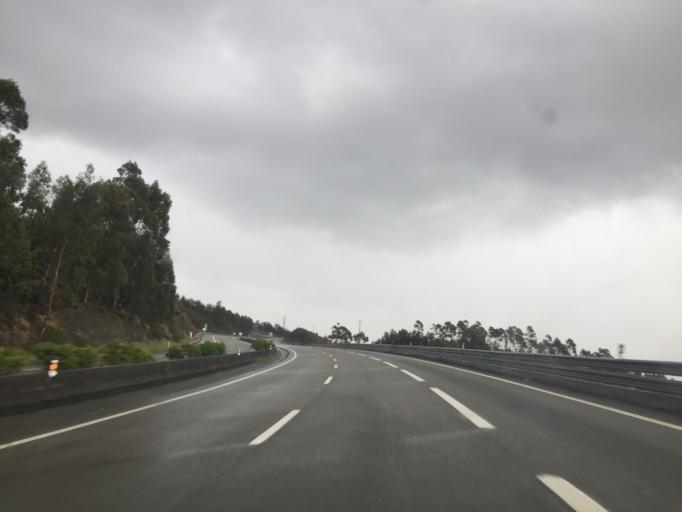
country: PT
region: Aveiro
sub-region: Agueda
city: Valongo
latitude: 40.6534
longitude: -8.3795
